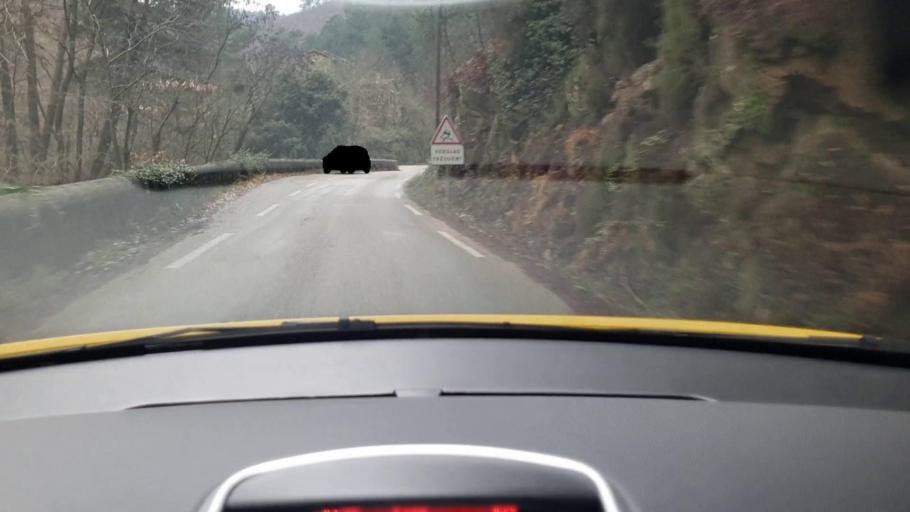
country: FR
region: Languedoc-Roussillon
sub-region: Departement du Gard
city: Besseges
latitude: 44.2775
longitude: 4.0734
